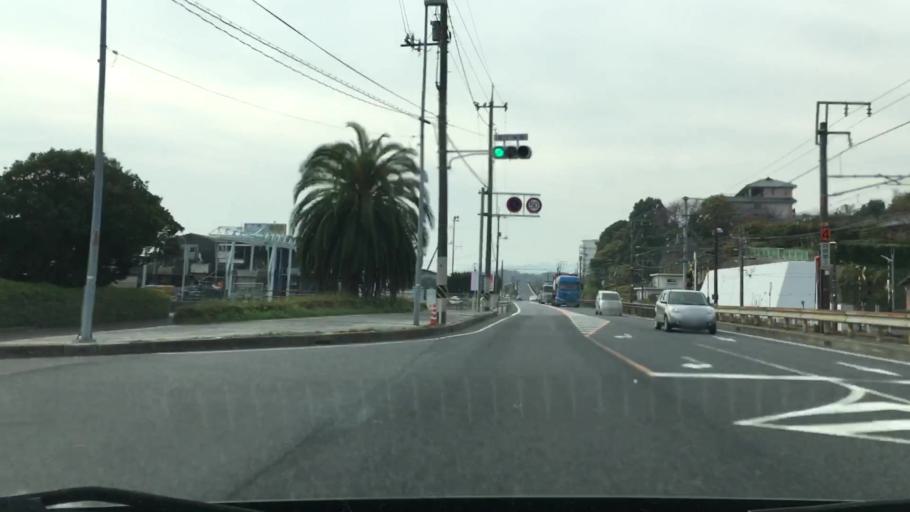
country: JP
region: Hiroshima
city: Ono-hara
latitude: 34.2743
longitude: 132.2601
